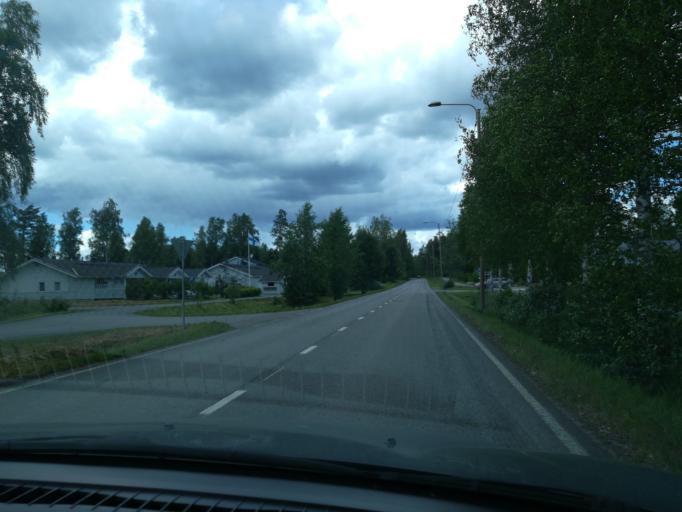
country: FI
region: Southern Savonia
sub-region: Mikkeli
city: Hirvensalmi
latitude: 61.6487
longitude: 26.7716
